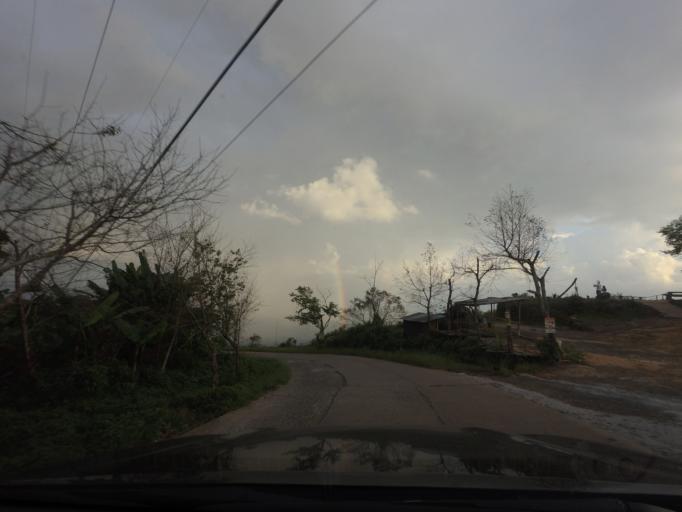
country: TH
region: Phetchabun
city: Lom Kao
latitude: 16.8938
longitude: 101.1031
